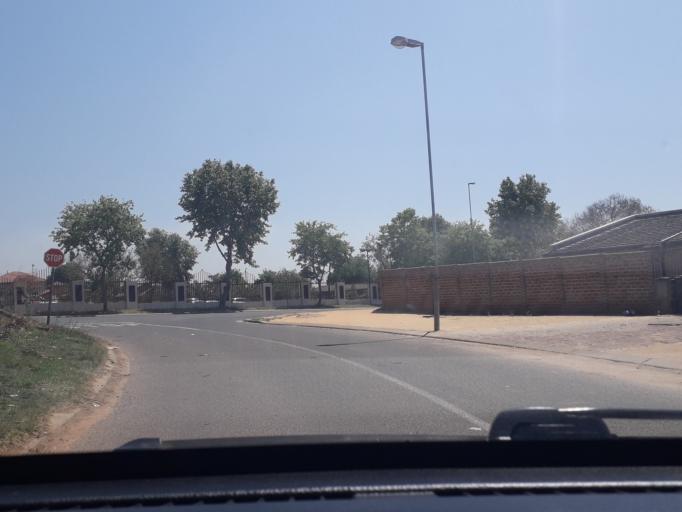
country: ZA
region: Gauteng
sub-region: City of Johannesburg Metropolitan Municipality
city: Modderfontein
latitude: -26.0934
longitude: 28.0955
